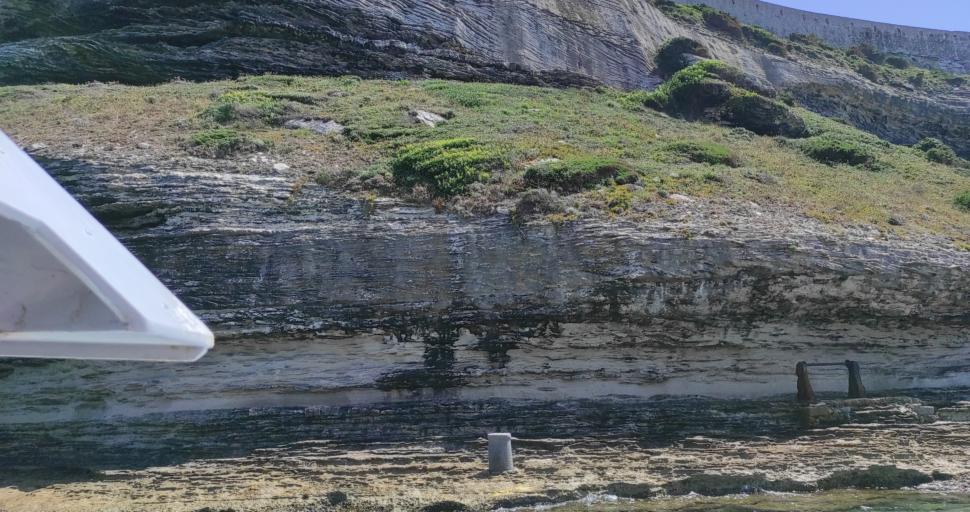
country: FR
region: Corsica
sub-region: Departement de la Corse-du-Sud
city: Bonifacio
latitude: 41.3887
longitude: 9.1502
